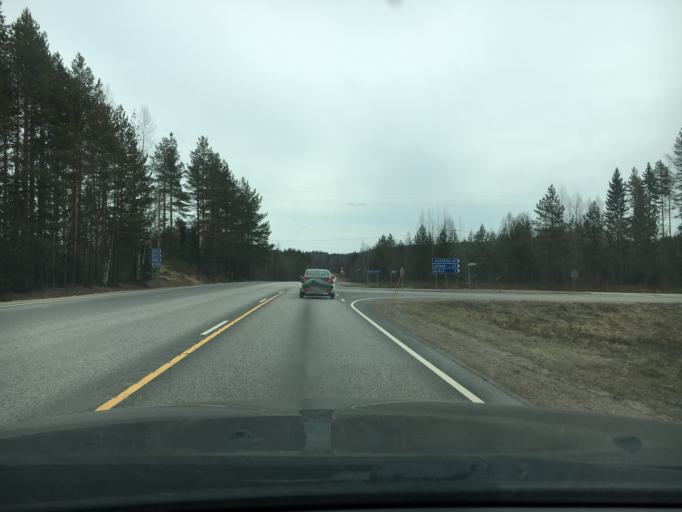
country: FI
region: Central Finland
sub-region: AEaenekoski
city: Sumiainen
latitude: 62.5685
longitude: 26.0640
